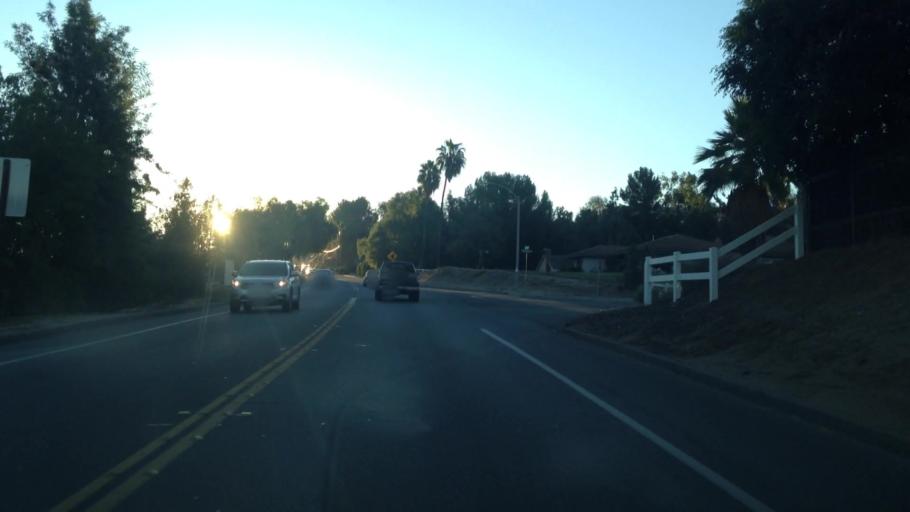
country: US
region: California
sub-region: Riverside County
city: Woodcrest
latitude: 33.8939
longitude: -117.3773
